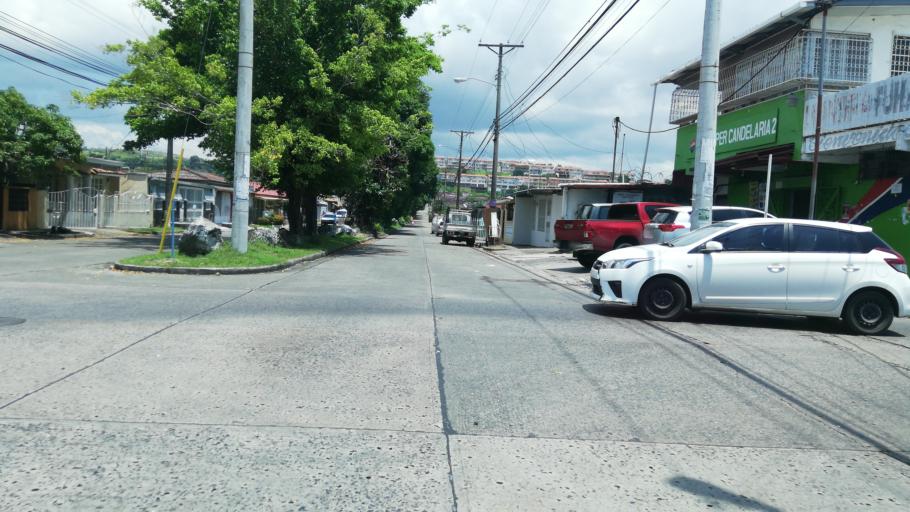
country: PA
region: Panama
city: San Miguelito
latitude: 9.0570
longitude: -79.4560
